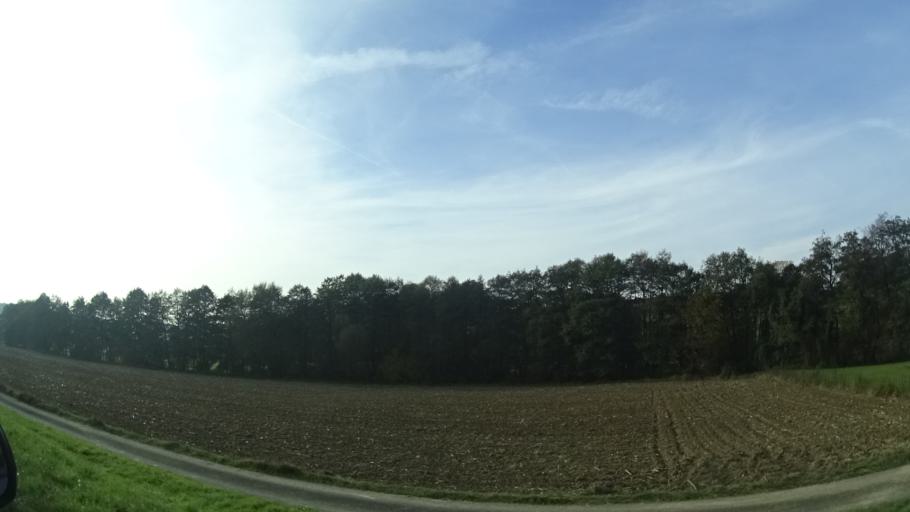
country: DE
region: Baden-Wuerttemberg
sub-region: Karlsruhe Region
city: Billigheim
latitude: 49.4039
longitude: 9.2331
